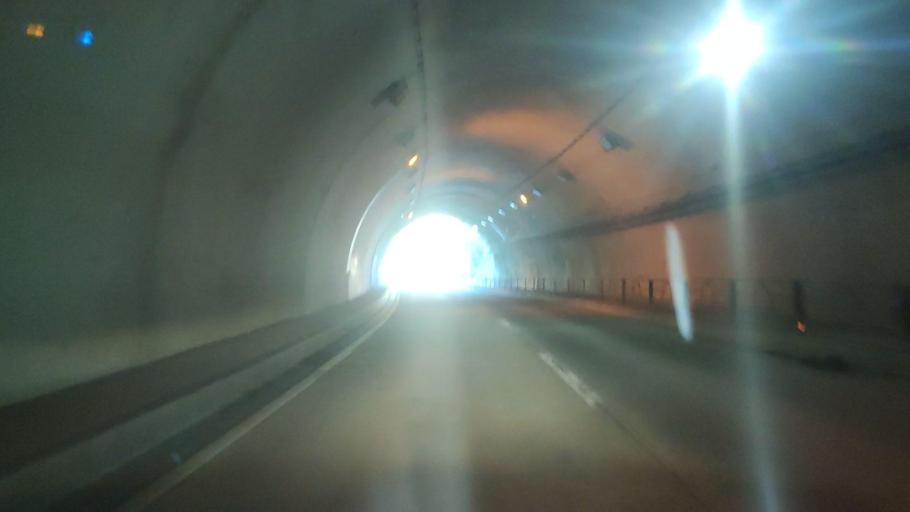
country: JP
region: Miyazaki
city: Nobeoka
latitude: 32.6940
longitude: 131.8117
